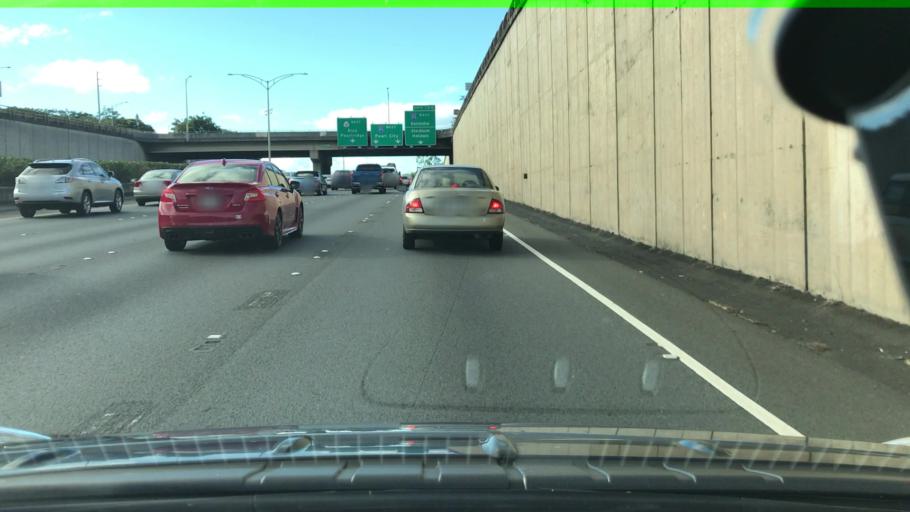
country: US
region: Hawaii
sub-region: Honolulu County
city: Halawa Heights
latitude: 21.3657
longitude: -157.9033
